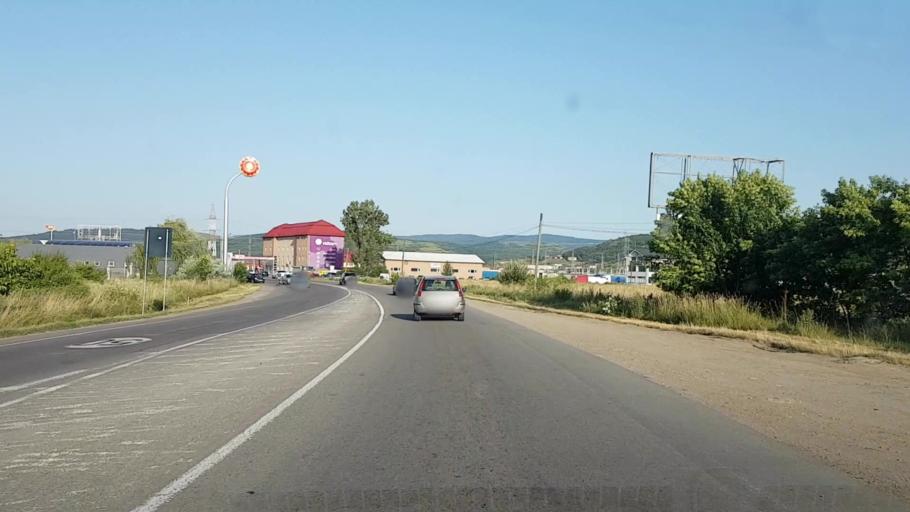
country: RO
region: Cluj
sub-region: Comuna Floresti
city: Luna de Sus
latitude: 46.7449
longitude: 23.4527
